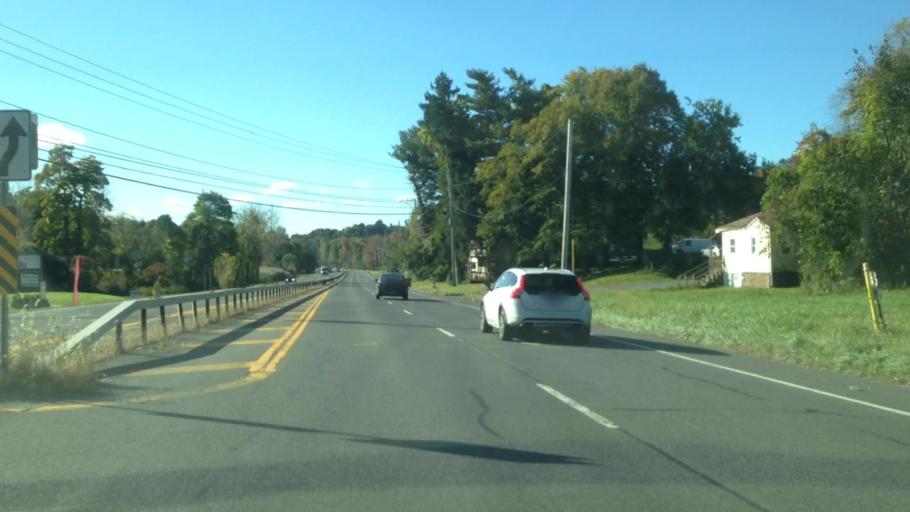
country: US
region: New York
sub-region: Ulster County
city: Highland
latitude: 41.7499
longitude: -73.9644
